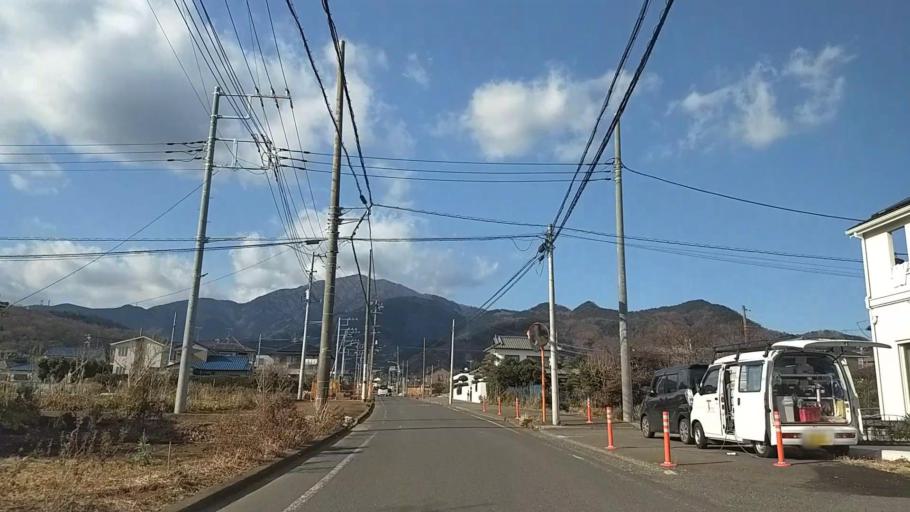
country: JP
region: Kanagawa
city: Isehara
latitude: 35.4108
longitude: 139.2890
